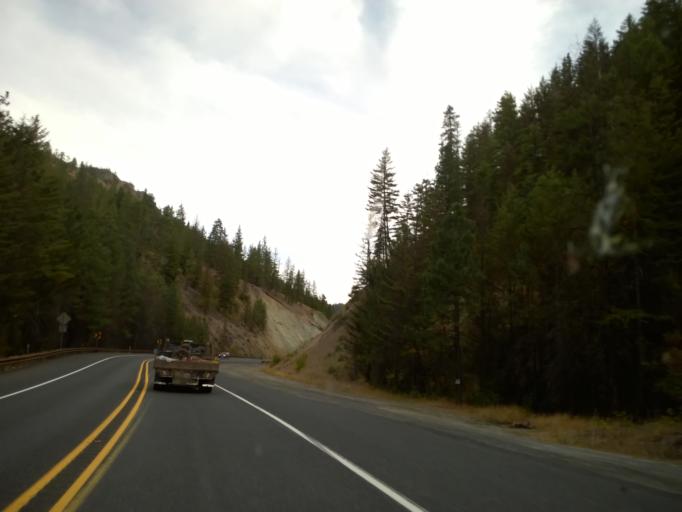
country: US
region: Washington
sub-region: Chelan County
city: Leavenworth
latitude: 47.4159
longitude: -120.6589
